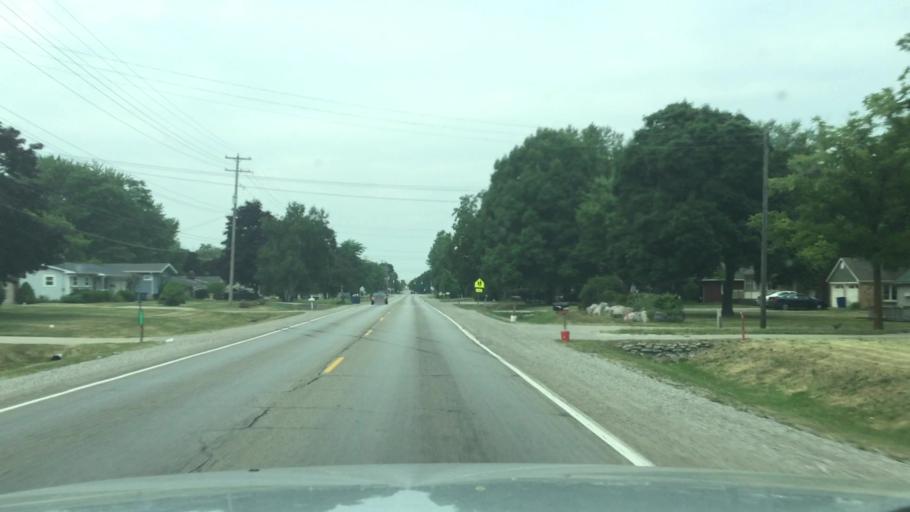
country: US
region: Michigan
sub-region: Genesee County
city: Flint
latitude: 42.9594
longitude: -83.7077
